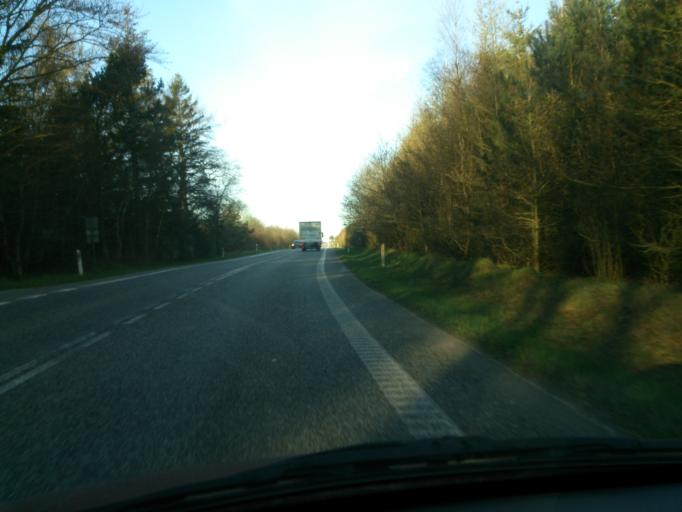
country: DK
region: Central Jutland
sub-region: Viborg Kommune
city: Bjerringbro
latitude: 56.4428
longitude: 9.7077
